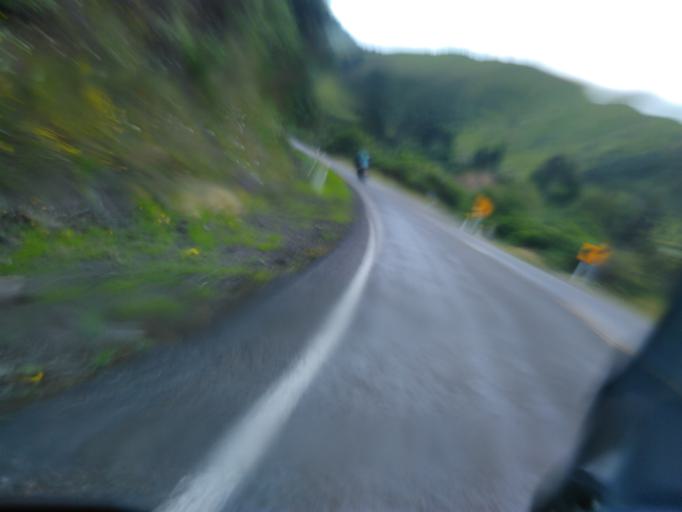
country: NZ
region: Bay of Plenty
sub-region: Opotiki District
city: Opotiki
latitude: -38.2545
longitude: 177.2987
